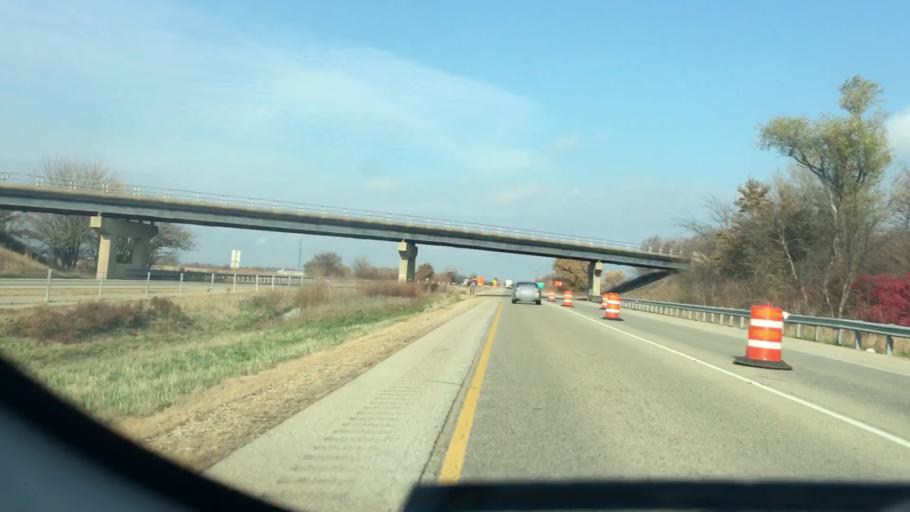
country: US
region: Illinois
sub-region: McLean County
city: Danvers
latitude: 40.5757
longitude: -89.1324
